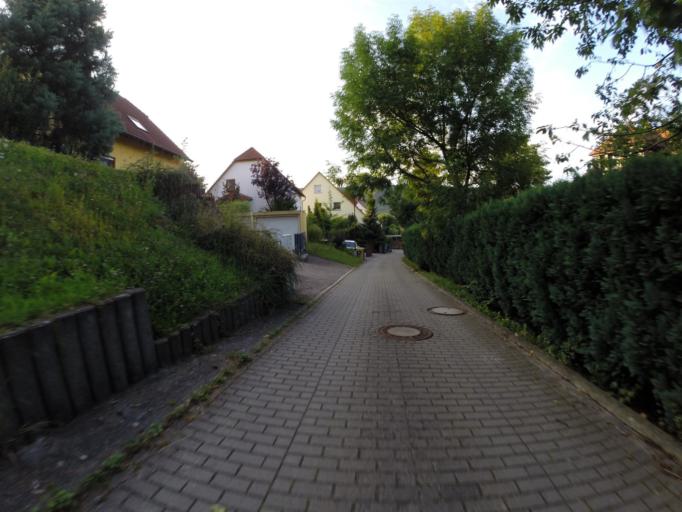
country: DE
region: Thuringia
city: Grosslobichau
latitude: 50.9264
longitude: 11.6500
